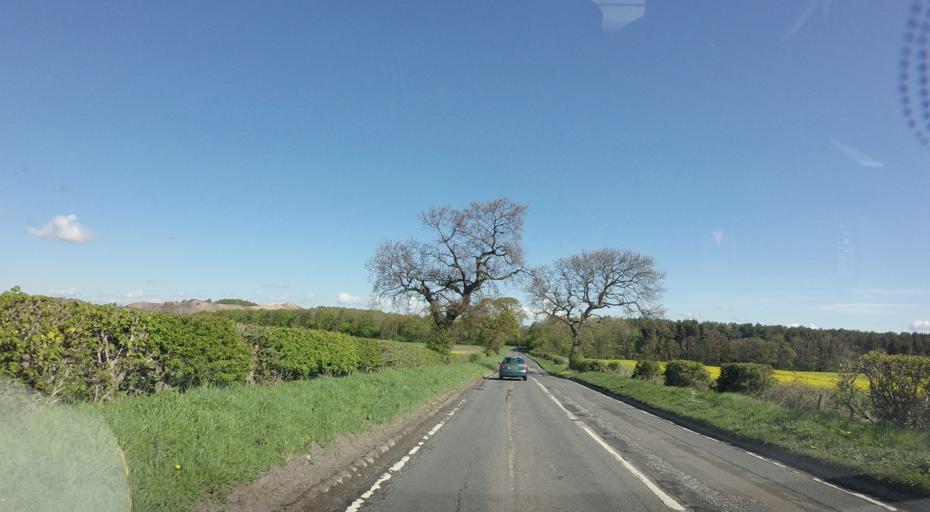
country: GB
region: Scotland
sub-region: West Lothian
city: Broxburn
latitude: 55.9680
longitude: -3.5073
